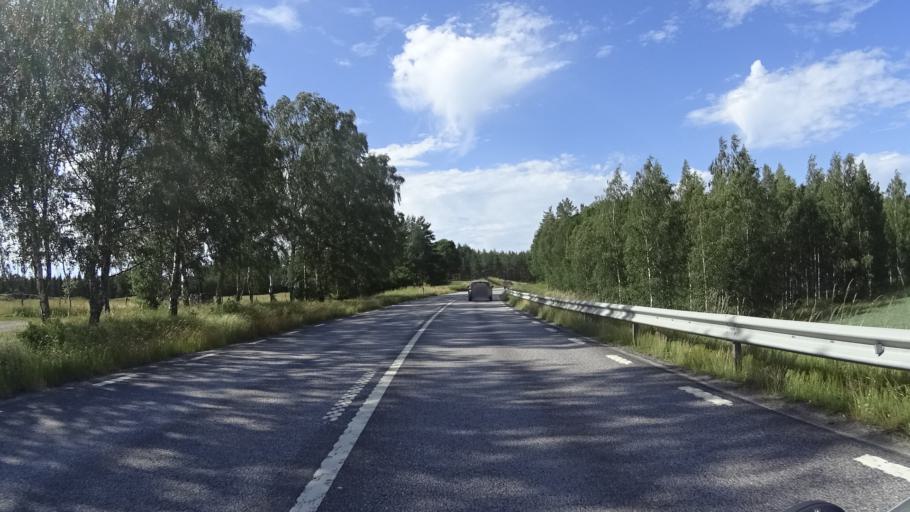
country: SE
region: OEstergoetland
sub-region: Linkopings Kommun
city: Sturefors
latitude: 58.3228
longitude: 15.8624
